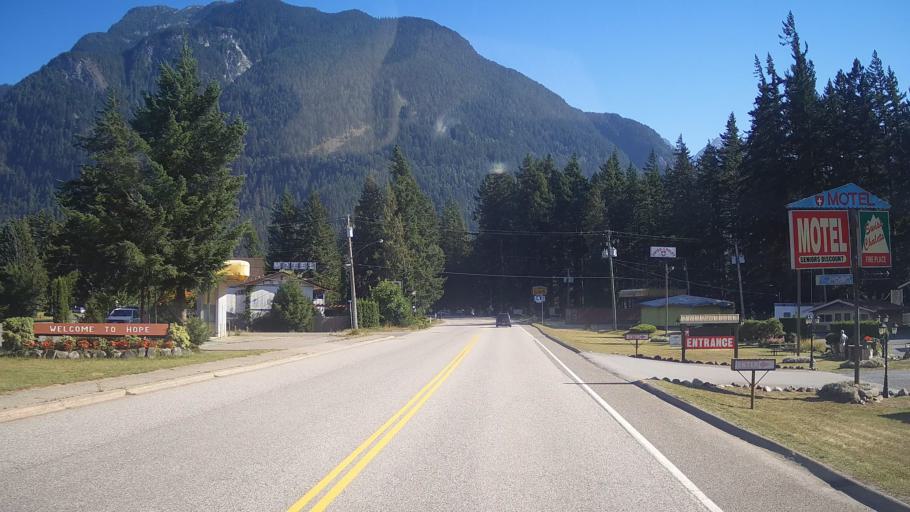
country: CA
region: British Columbia
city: Hope
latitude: 49.3842
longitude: -121.4479
